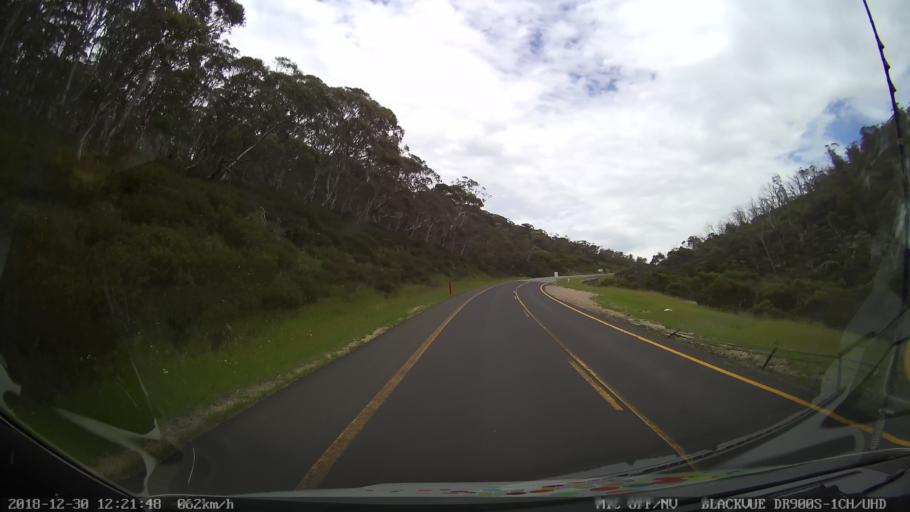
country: AU
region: New South Wales
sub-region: Snowy River
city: Jindabyne
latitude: -36.3546
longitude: 148.5153
